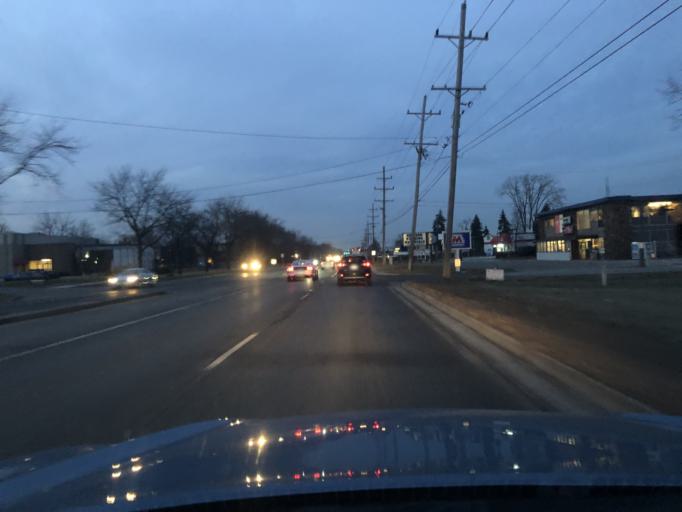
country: US
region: Illinois
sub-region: Cook County
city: Elk Grove Village
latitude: 42.0277
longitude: -87.9600
